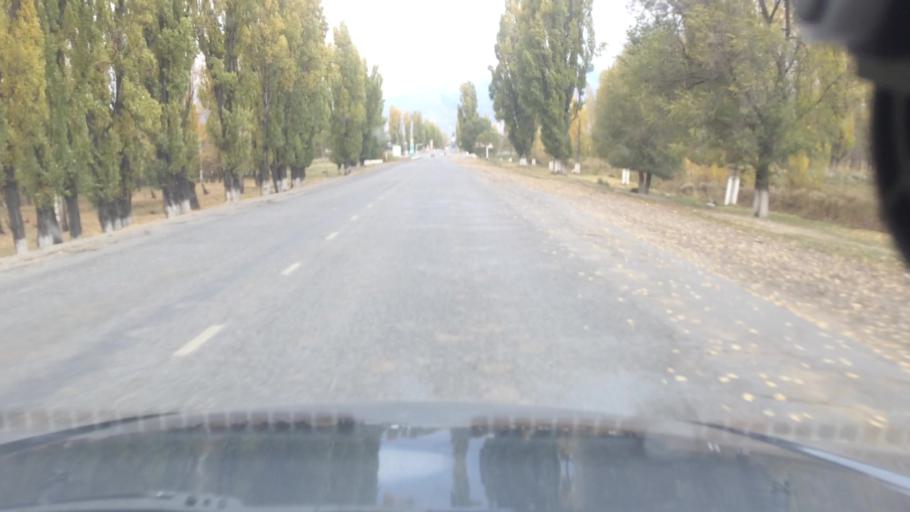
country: KG
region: Ysyk-Koel
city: Tyup
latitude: 42.7366
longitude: 78.3492
